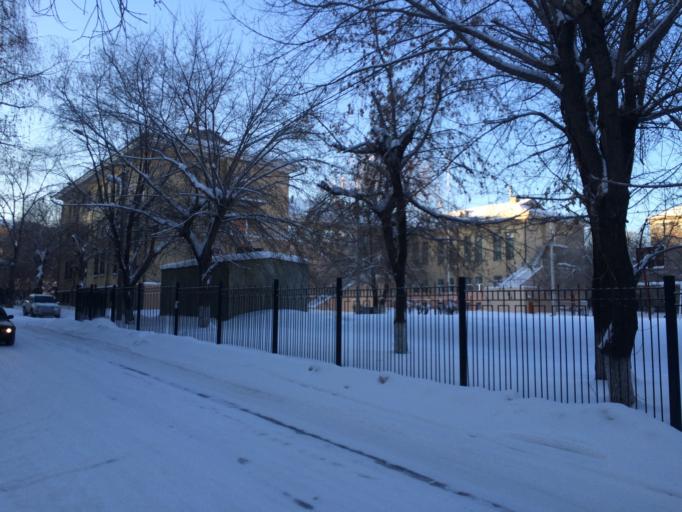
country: RU
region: Chelyabinsk
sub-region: Gorod Magnitogorsk
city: Magnitogorsk
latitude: 53.4150
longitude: 58.9866
